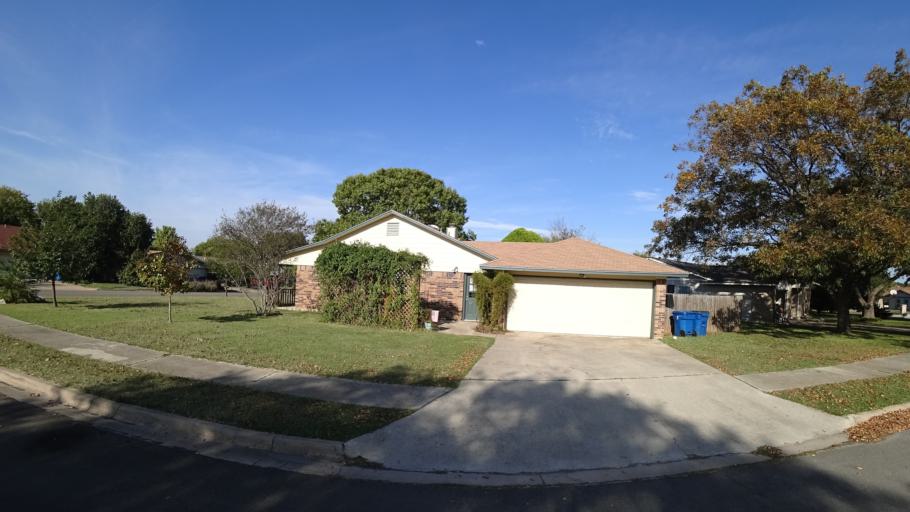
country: US
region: Texas
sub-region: Williamson County
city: Anderson Mill
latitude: 30.4554
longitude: -97.8113
